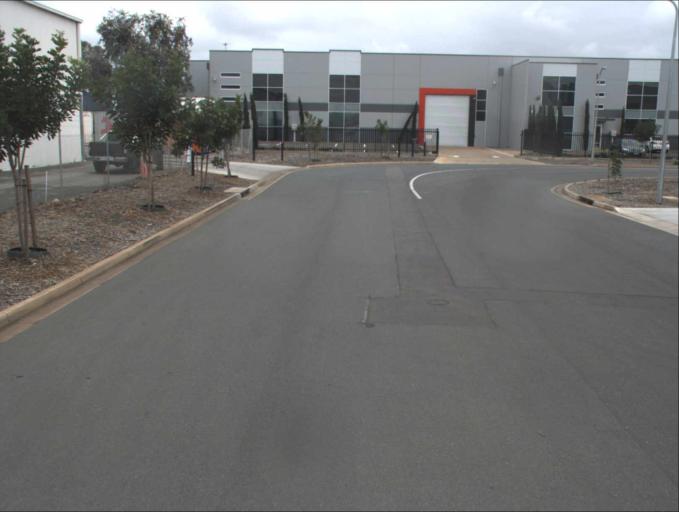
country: AU
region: South Australia
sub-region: Prospect
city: Prospect
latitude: -34.8790
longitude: 138.5799
